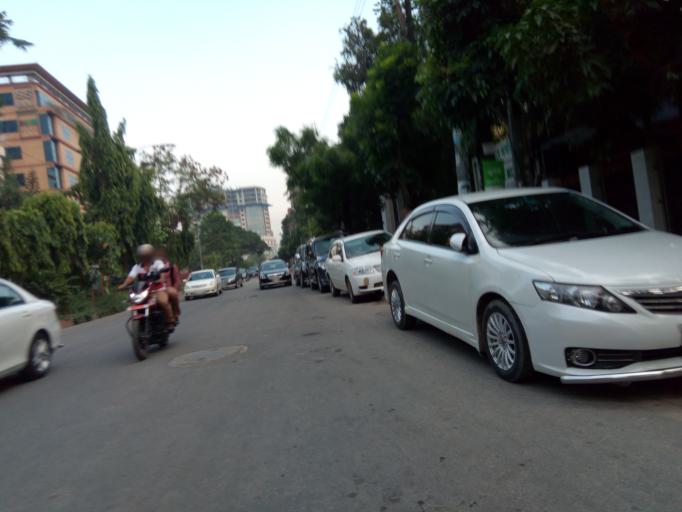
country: BD
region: Dhaka
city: Paltan
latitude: 23.7766
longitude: 90.4162
